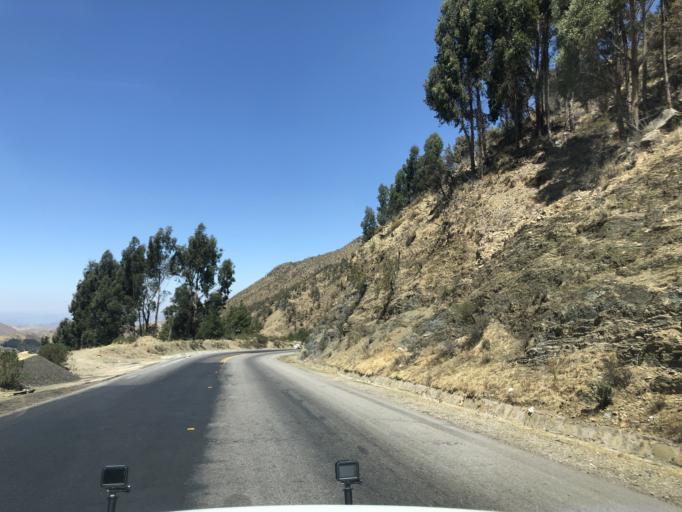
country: BO
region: Cochabamba
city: Irpa Irpa
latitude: -17.6624
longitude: -66.4502
